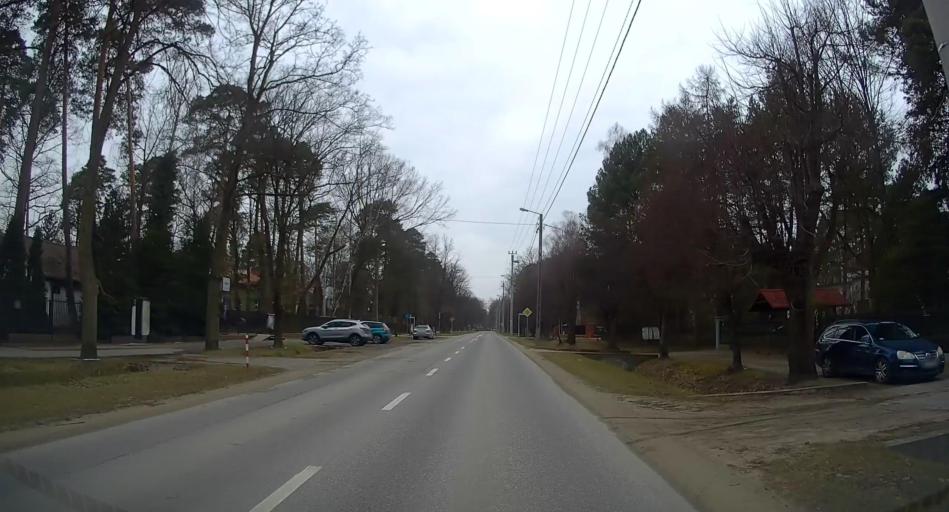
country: PL
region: Masovian Voivodeship
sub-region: Powiat piaseczynski
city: Piaseczno
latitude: 52.0610
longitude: 21.0068
